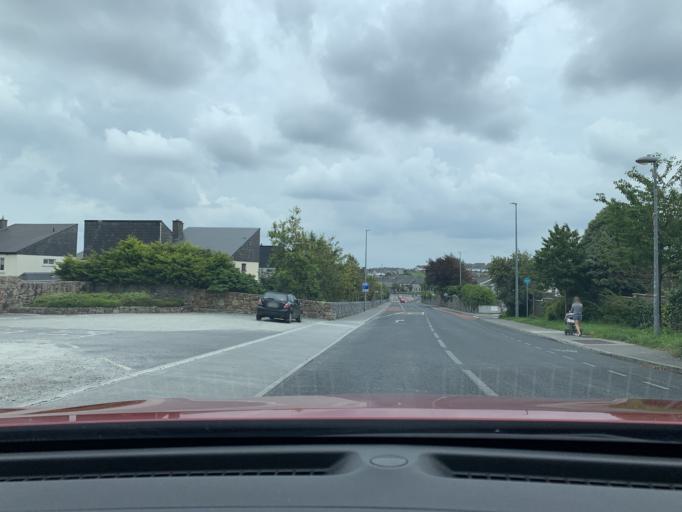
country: IE
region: Connaught
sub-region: County Galway
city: Gaillimh
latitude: 53.2746
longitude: -9.0892
